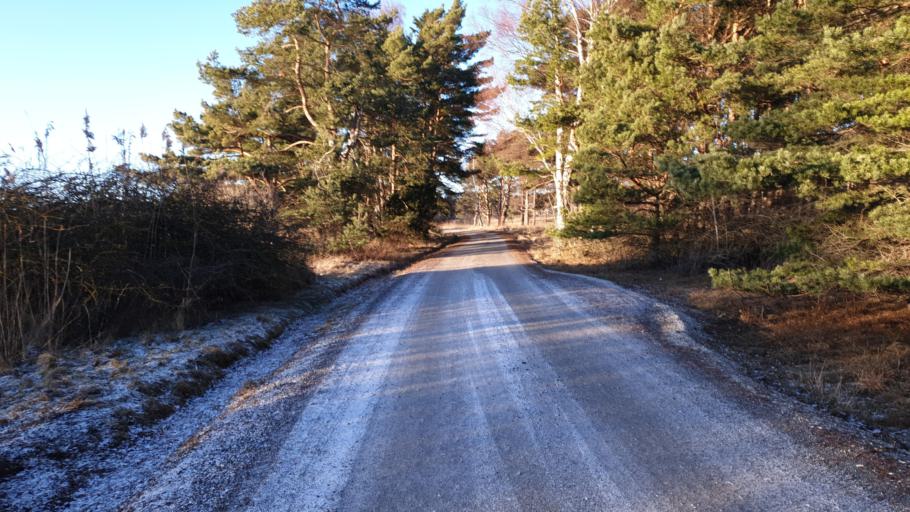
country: SE
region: Gotland
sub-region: Gotland
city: Slite
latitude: 57.3730
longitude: 18.8056
